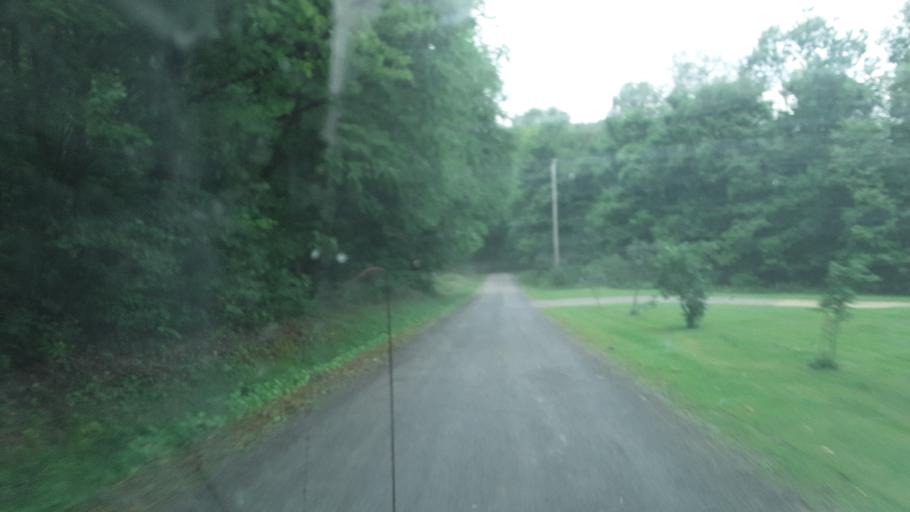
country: US
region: Pennsylvania
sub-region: Jefferson County
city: Punxsutawney
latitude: 40.9489
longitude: -79.1499
